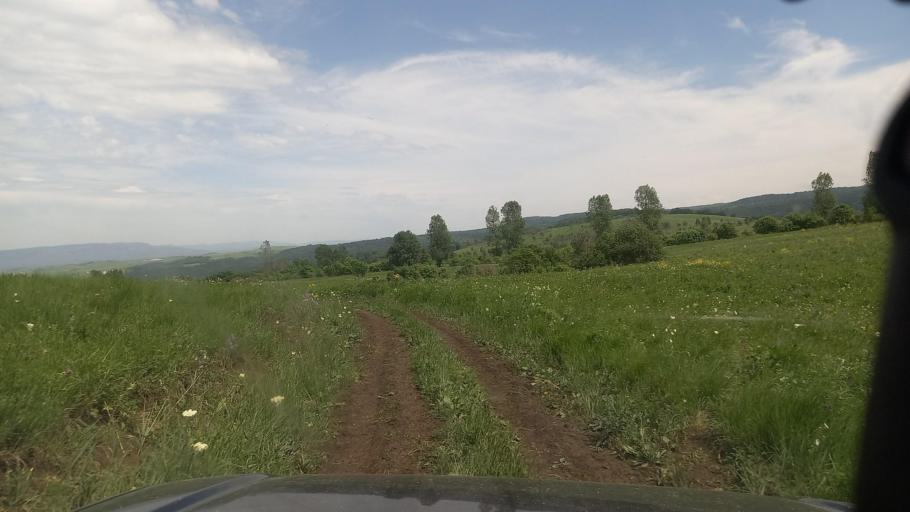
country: RU
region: Karachayevo-Cherkesiya
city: Pregradnaya
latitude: 44.0667
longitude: 41.3051
